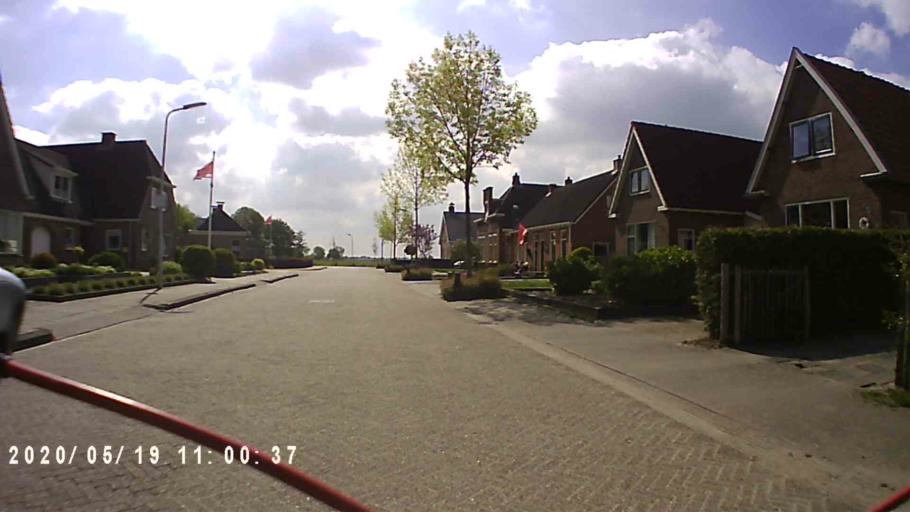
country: NL
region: Groningen
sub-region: Gemeente Zuidhorn
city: Grijpskerk
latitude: 53.3037
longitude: 6.2692
